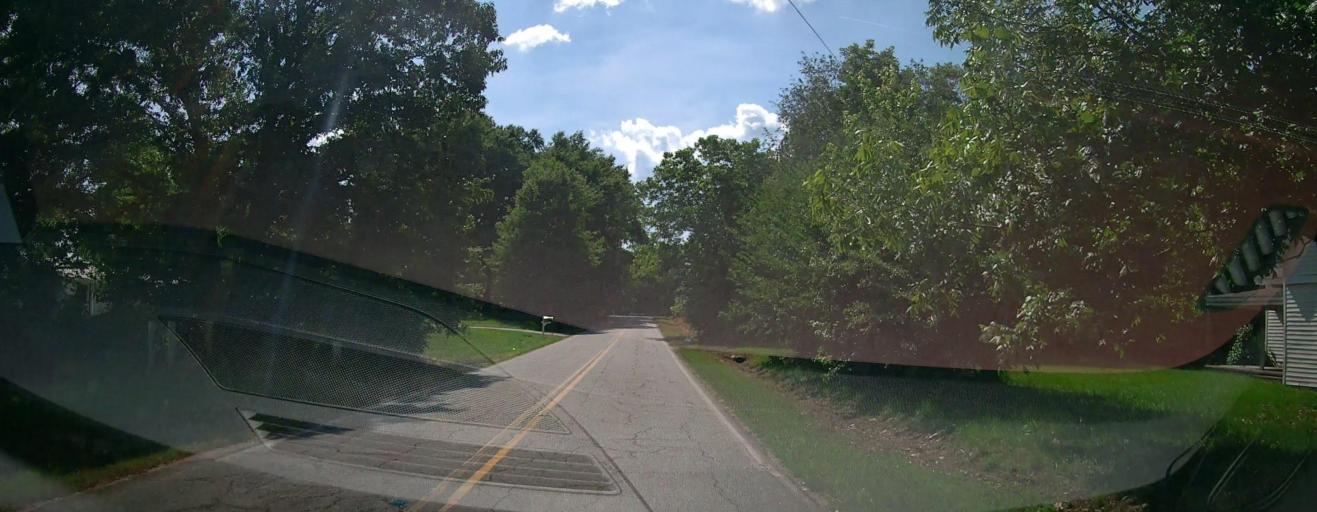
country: US
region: Georgia
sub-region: Spalding County
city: East Griffin
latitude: 33.2325
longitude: -84.1425
